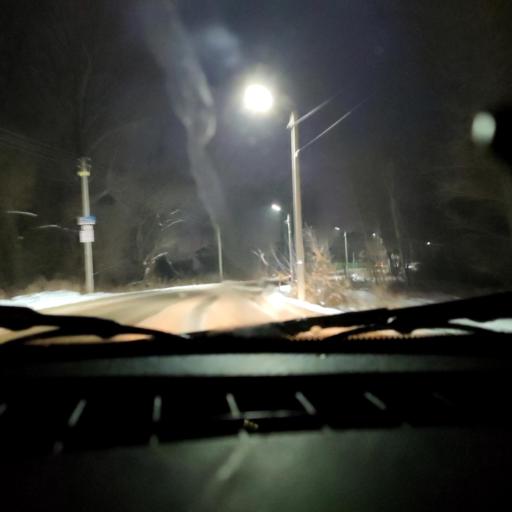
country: RU
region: Bashkortostan
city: Ufa
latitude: 54.6613
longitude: 56.0682
